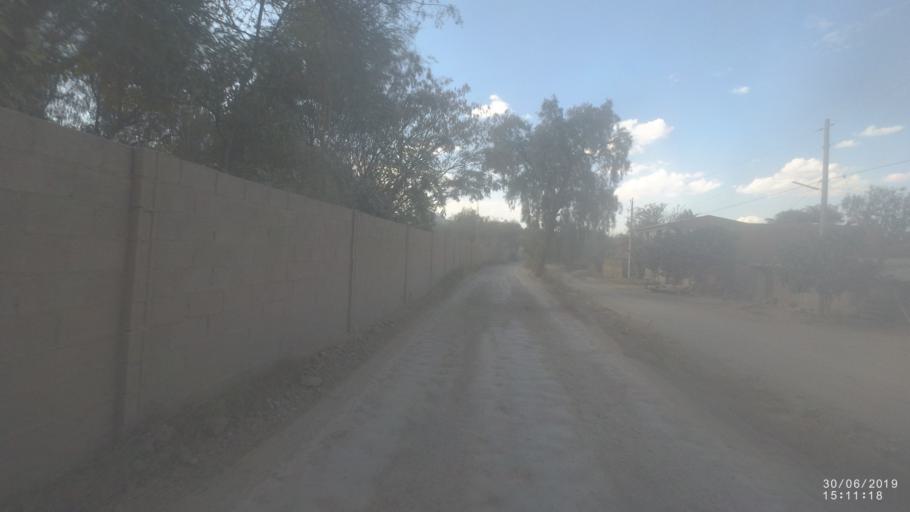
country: BO
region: Cochabamba
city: Irpa Irpa
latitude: -17.7289
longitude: -66.2926
